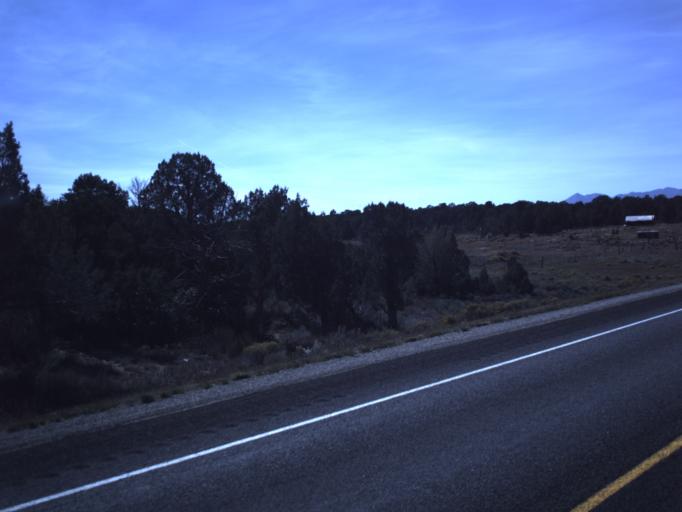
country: US
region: Colorado
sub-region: Dolores County
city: Dove Creek
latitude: 37.8249
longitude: -109.0712
